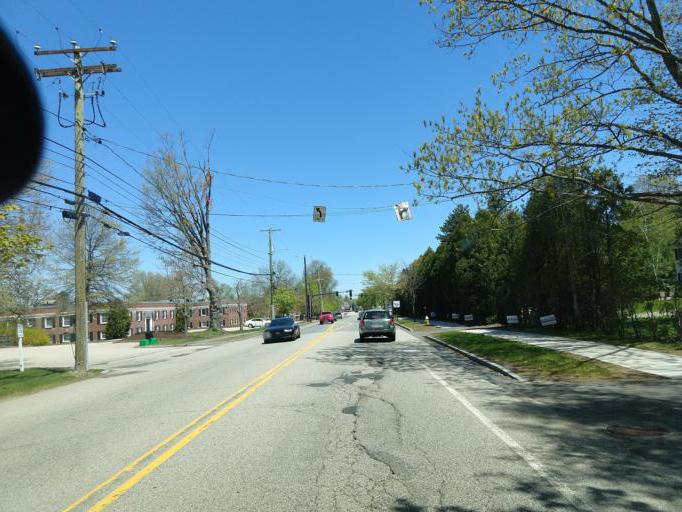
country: US
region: New Hampshire
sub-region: Rockingham County
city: Portsmouth
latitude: 43.0610
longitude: -70.7689
